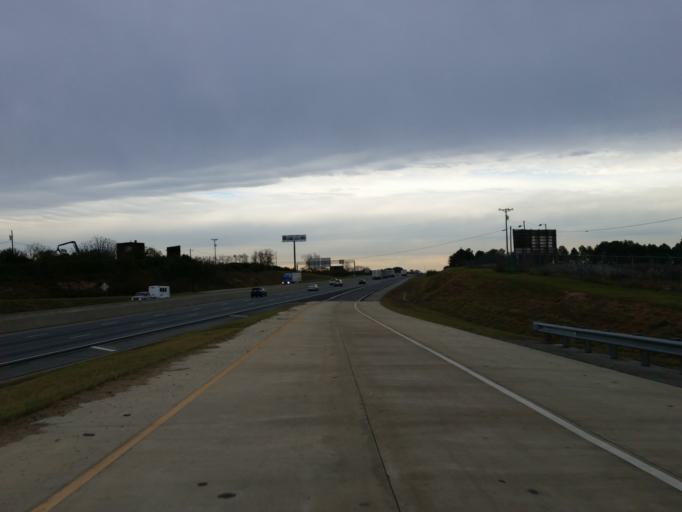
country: US
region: Georgia
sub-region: Turner County
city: Ashburn
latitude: 31.6650
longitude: -83.6077
